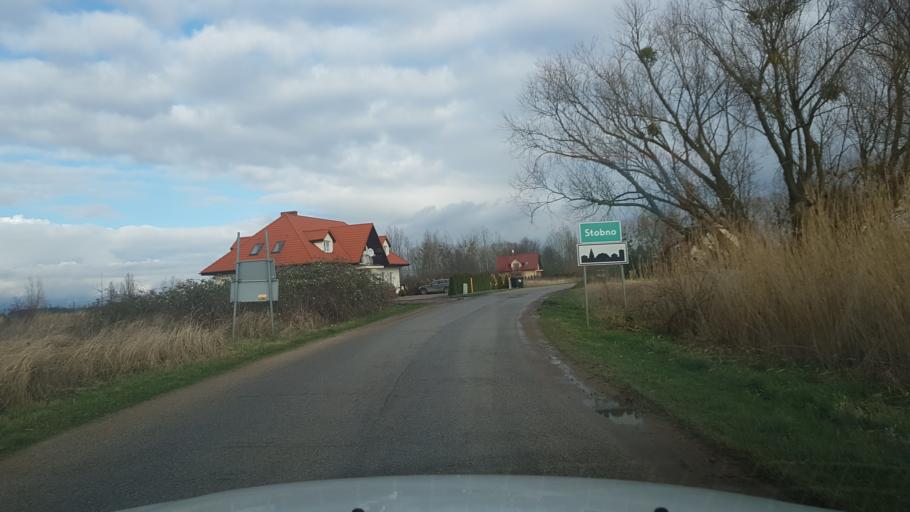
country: PL
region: West Pomeranian Voivodeship
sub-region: Powiat policki
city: Przeclaw
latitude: 53.4087
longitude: 14.4073
